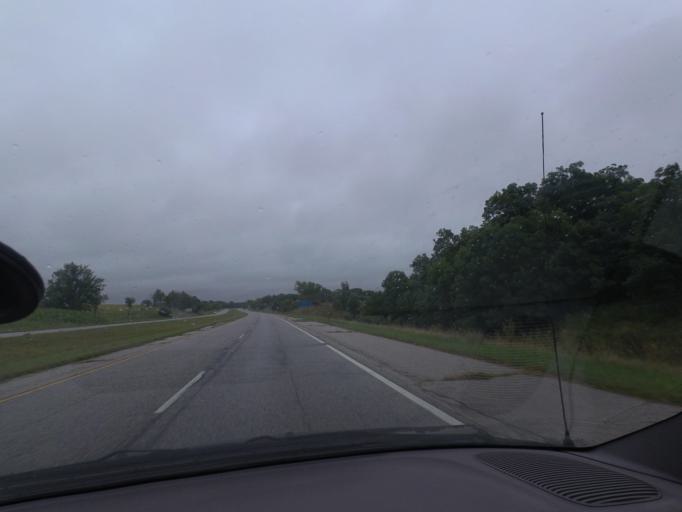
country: US
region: Illinois
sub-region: Pike County
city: Pittsfield
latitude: 39.6720
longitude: -90.7907
